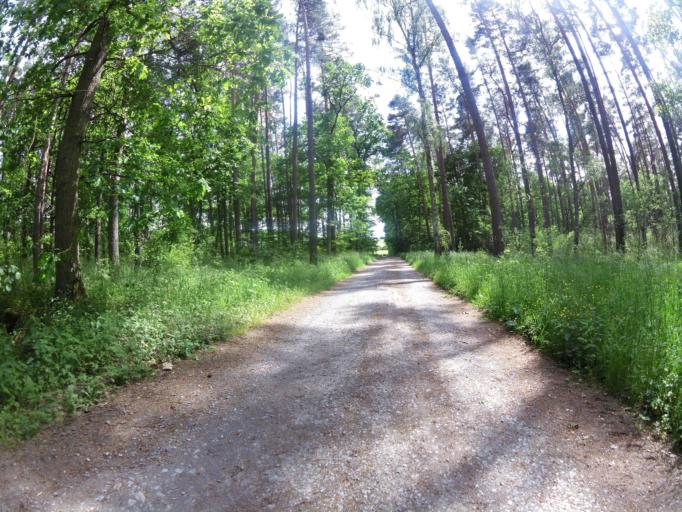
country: DE
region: Bavaria
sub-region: Regierungsbezirk Unterfranken
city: Sommerhausen
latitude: 49.6952
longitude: 10.0553
